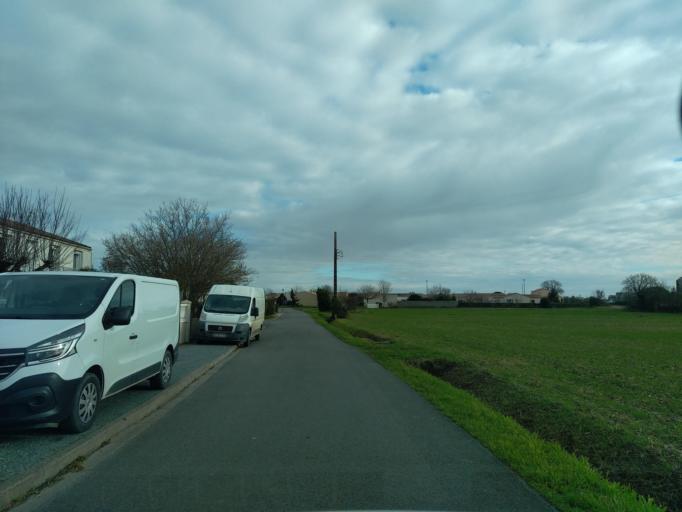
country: FR
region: Pays de la Loire
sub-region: Departement de la Vendee
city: Maillezais
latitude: 46.3404
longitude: -0.7812
